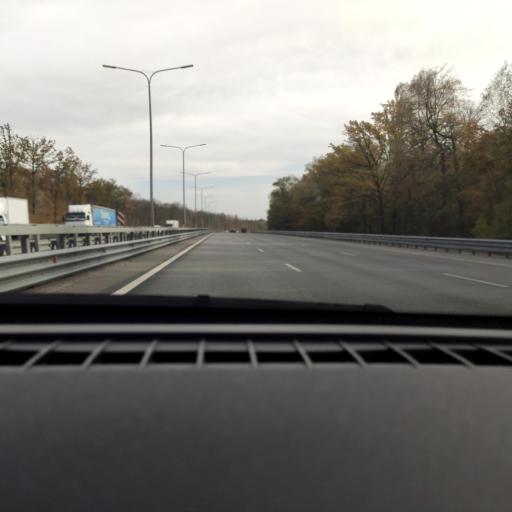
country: RU
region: Voronezj
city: Ramon'
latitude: 51.8329
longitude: 39.2358
